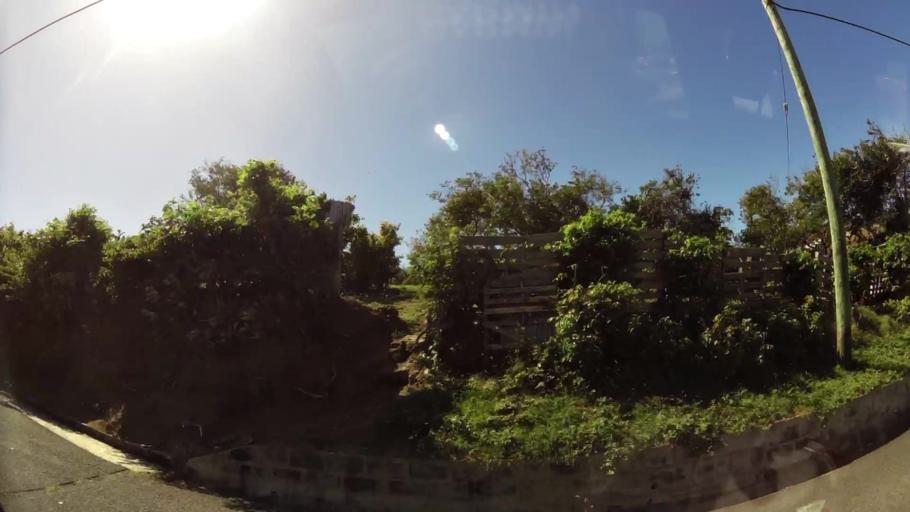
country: LC
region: Vieux-Fort
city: Vieux Fort
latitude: 13.7241
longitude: -60.9519
